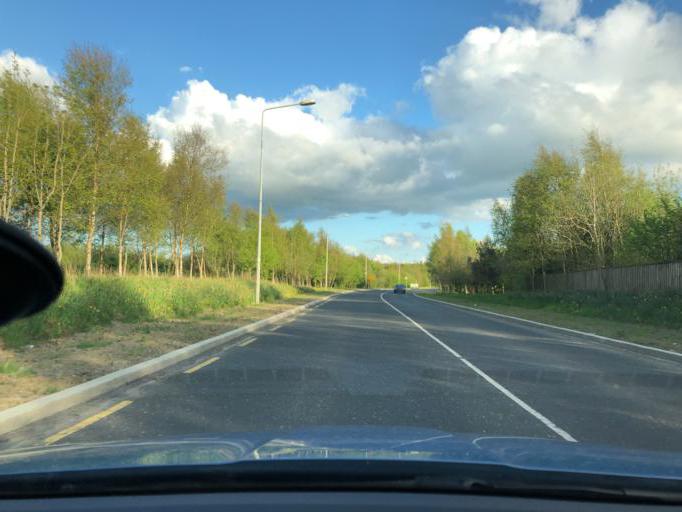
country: IE
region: Leinster
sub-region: Kildare
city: Kilcock
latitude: 53.3979
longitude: -6.6846
